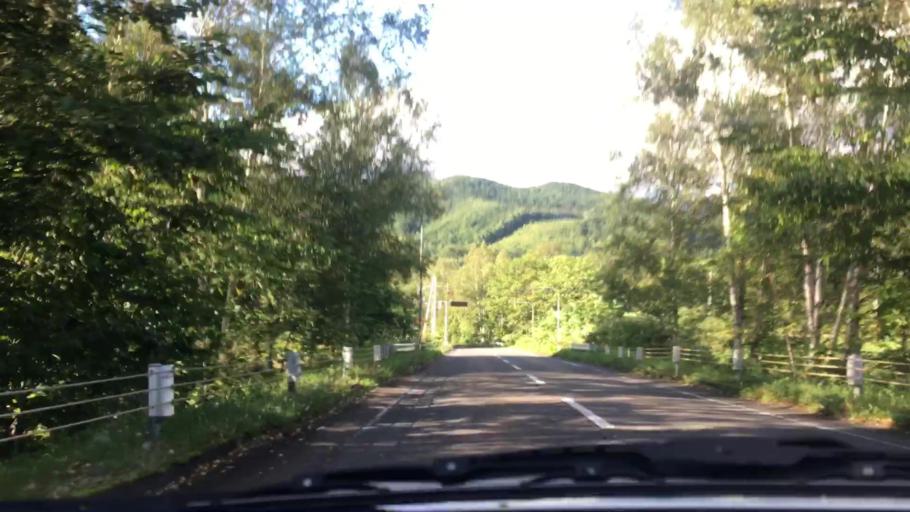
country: JP
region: Hokkaido
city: Otofuke
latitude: 43.1807
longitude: 142.9293
